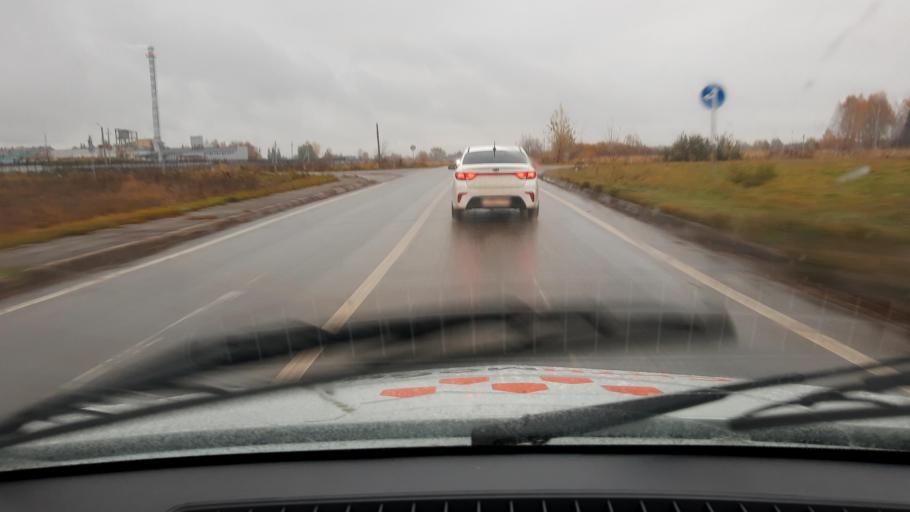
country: RU
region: Bashkortostan
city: Kabakovo
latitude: 54.7378
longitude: 56.2033
